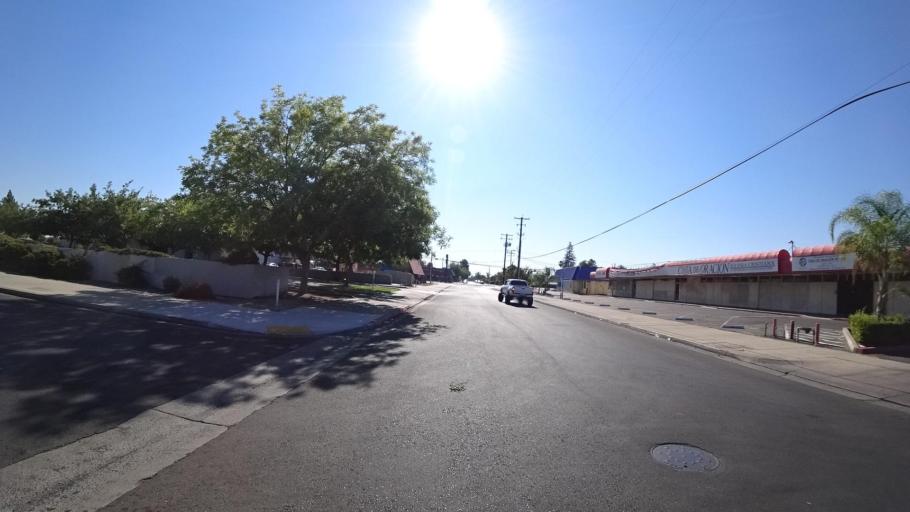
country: US
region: California
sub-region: Fresno County
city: Fresno
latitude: 36.7815
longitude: -119.7556
